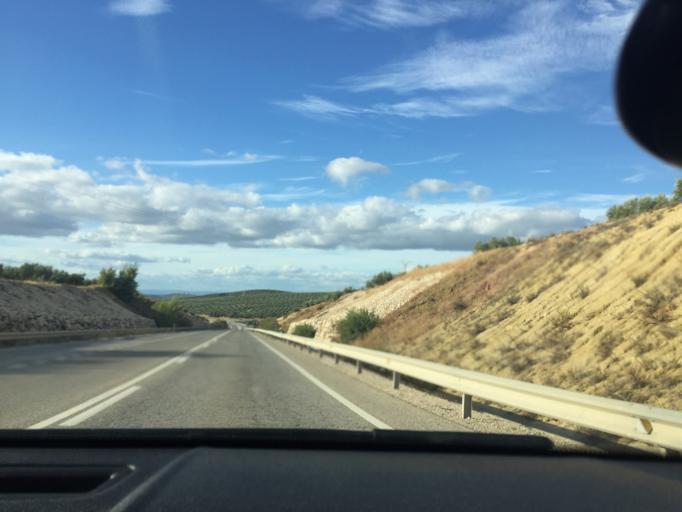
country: ES
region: Andalusia
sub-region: Provincia de Jaen
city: Torredonjimeno
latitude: 37.7636
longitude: -3.9677
